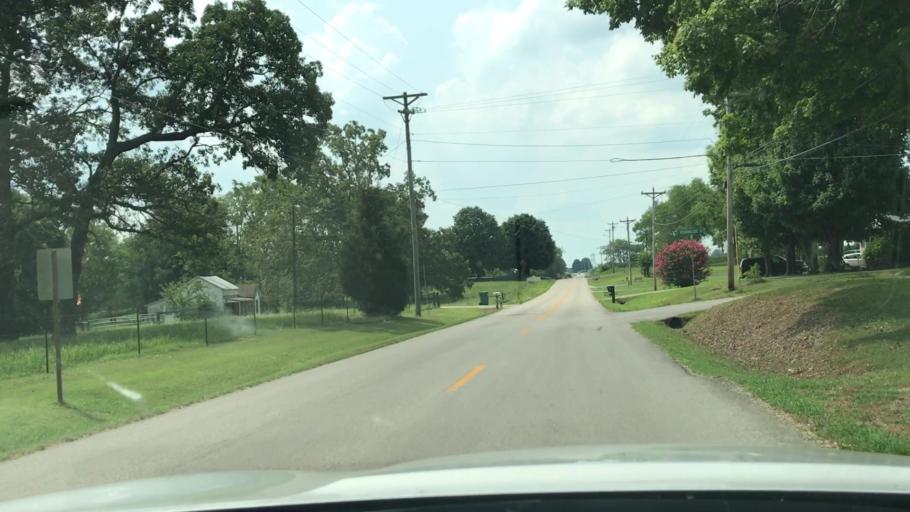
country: US
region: Kentucky
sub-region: Todd County
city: Elkton
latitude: 36.7999
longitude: -87.1488
